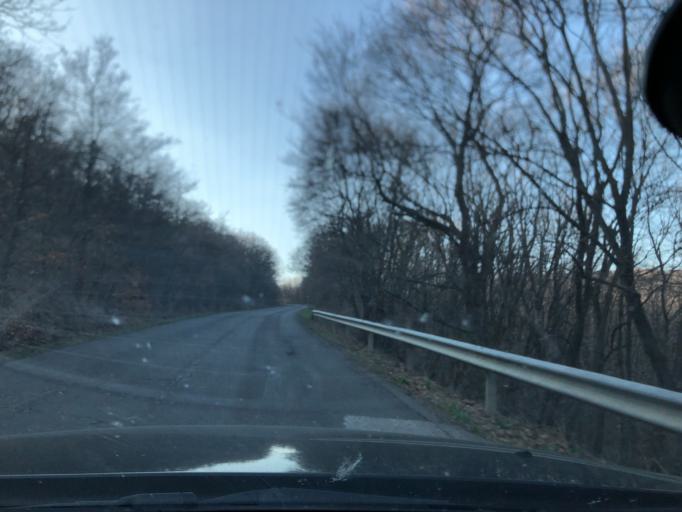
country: HU
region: Nograd
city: Paszto
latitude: 47.9160
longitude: 19.6386
